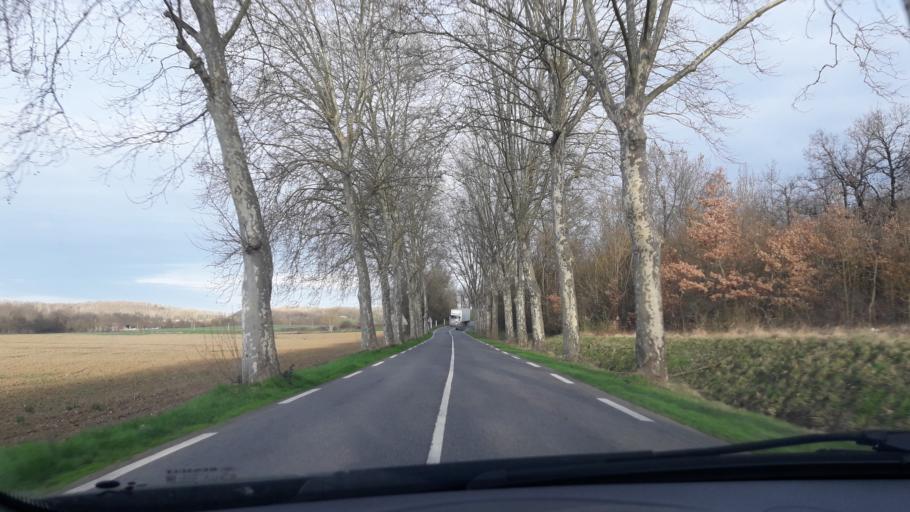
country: FR
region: Midi-Pyrenees
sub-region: Departement de la Haute-Garonne
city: Daux
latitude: 43.7209
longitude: 1.2476
